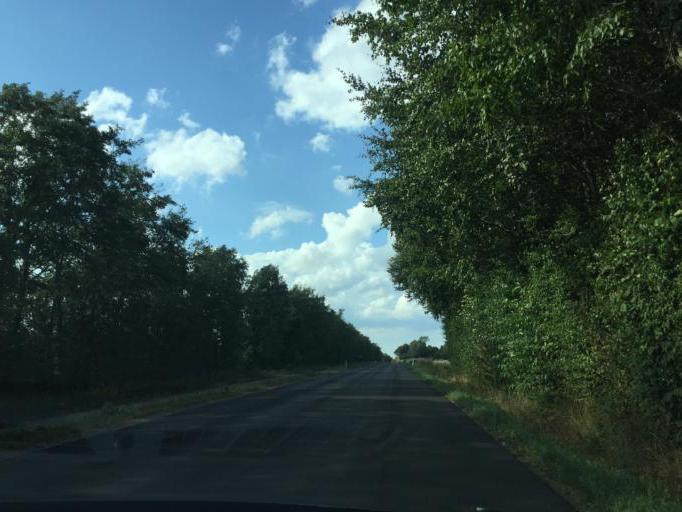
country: DK
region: South Denmark
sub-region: Faaborg-Midtfyn Kommune
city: Arslev
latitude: 55.3109
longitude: 10.4504
